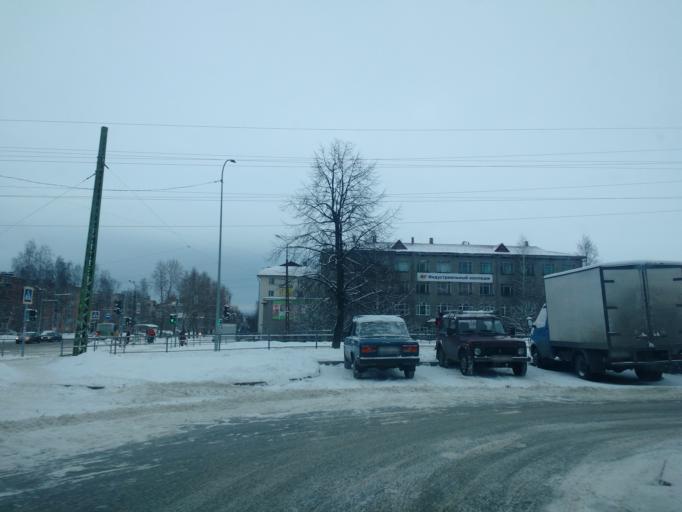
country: RU
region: Republic of Karelia
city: Petrozavodsk
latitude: 61.7955
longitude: 34.3545
